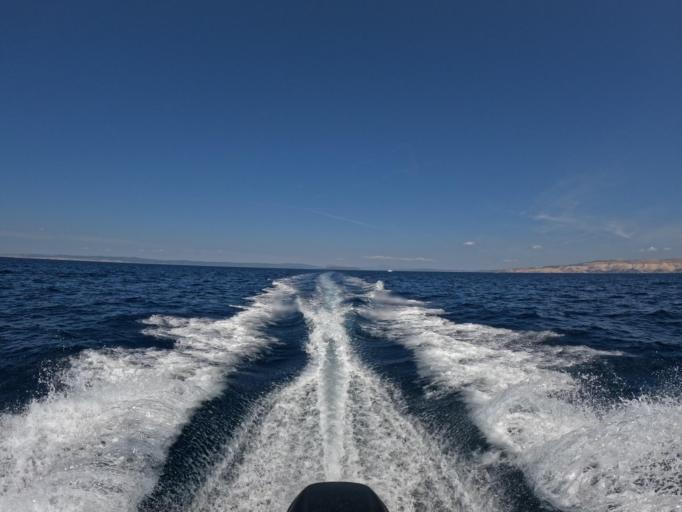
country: HR
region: Primorsko-Goranska
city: Lopar
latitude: 44.8685
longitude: 14.6743
